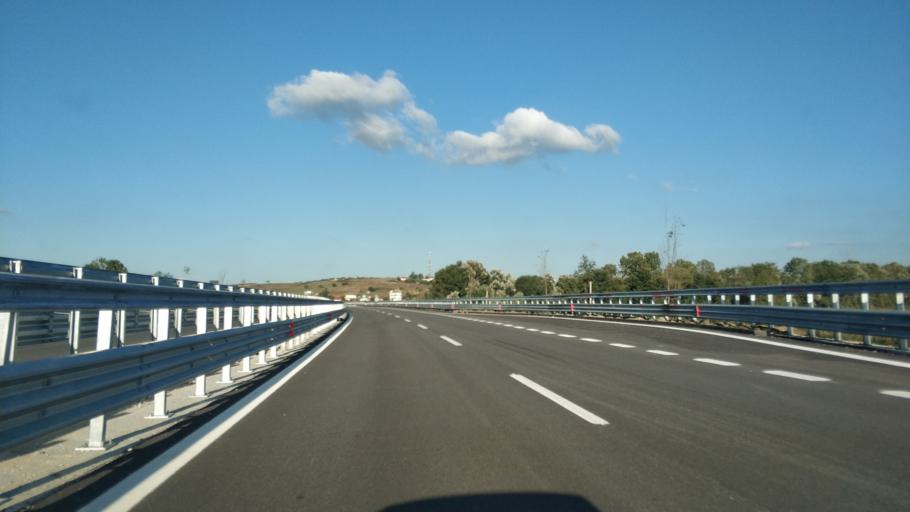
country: AL
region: Fier
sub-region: Rrethi i Fierit
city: Mbrostar-Ure
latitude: 40.7501
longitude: 19.5675
